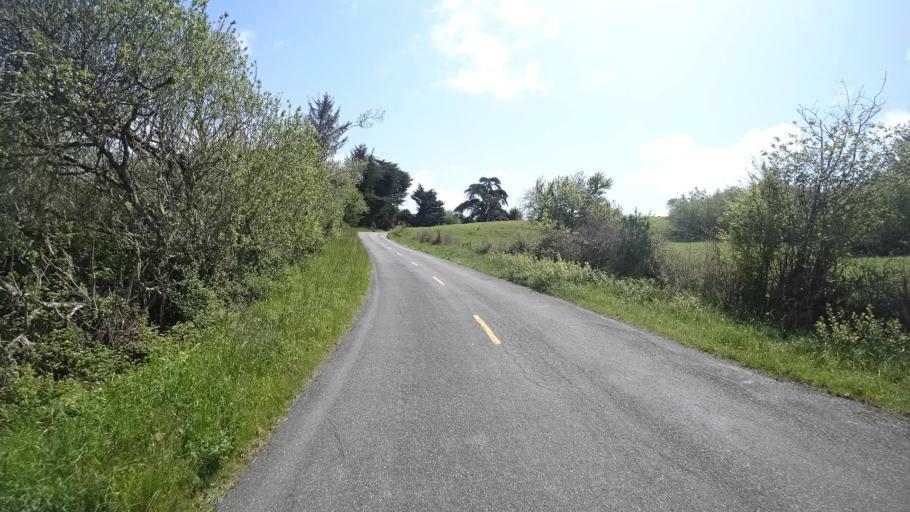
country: US
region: California
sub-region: Humboldt County
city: Humboldt Hill
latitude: 40.6764
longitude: -124.2253
